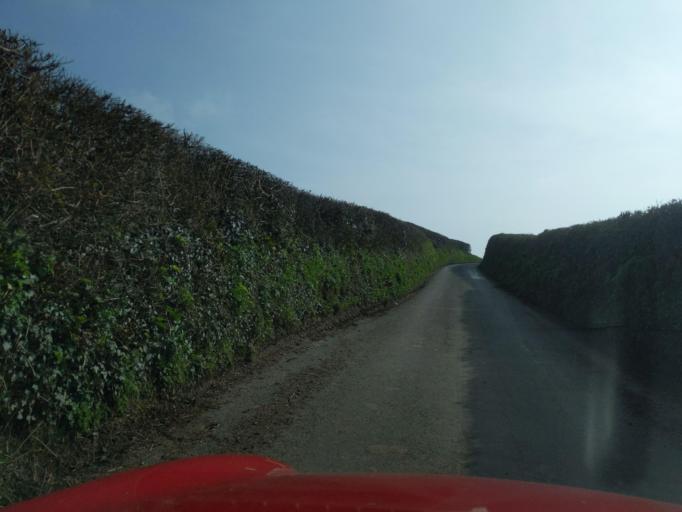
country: GB
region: England
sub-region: Devon
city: Salcombe
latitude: 50.2568
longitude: -3.7141
